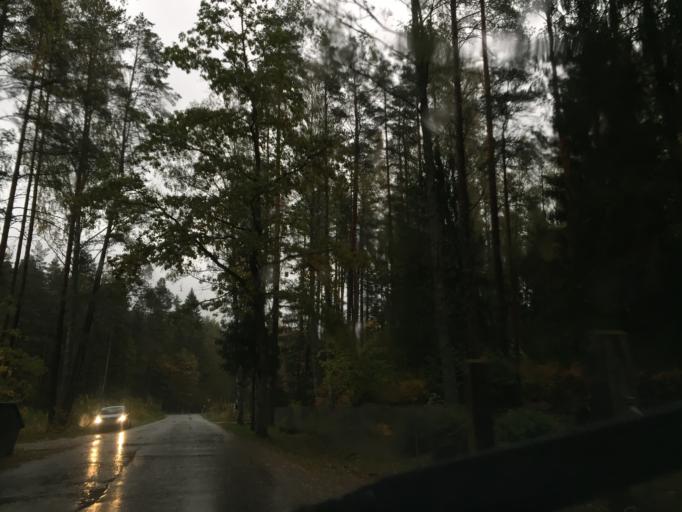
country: LV
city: Tireli
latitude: 56.9319
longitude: 23.4793
